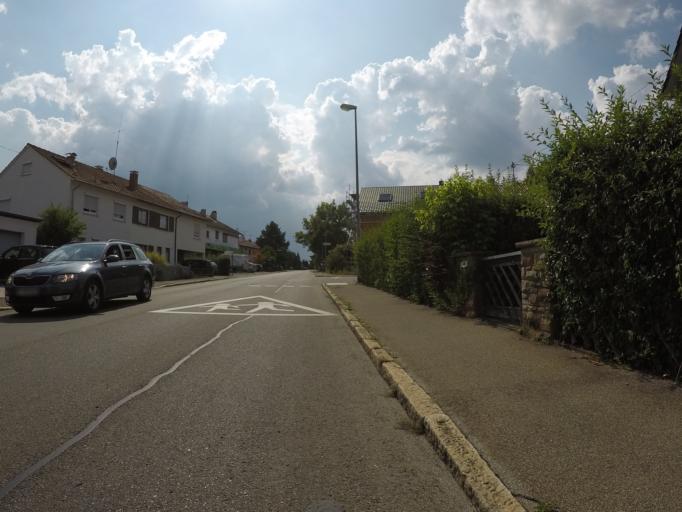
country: DE
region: Baden-Wuerttemberg
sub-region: Tuebingen Region
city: Eningen unter Achalm
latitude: 48.4837
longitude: 9.2460
